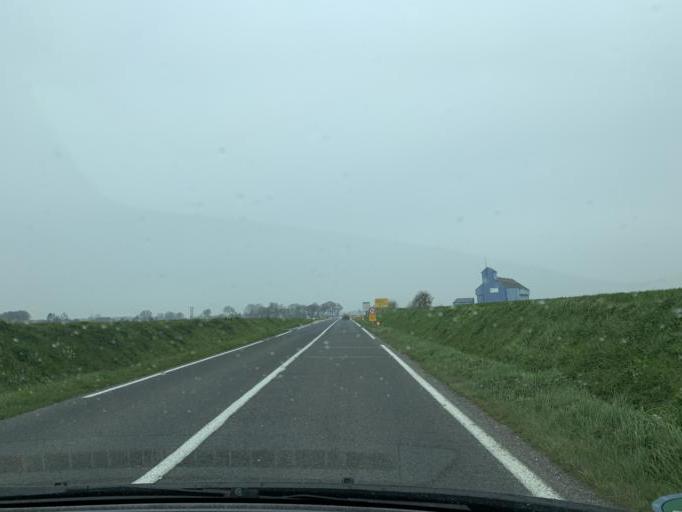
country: FR
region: Haute-Normandie
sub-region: Departement de la Seine-Maritime
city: Neville
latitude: 49.8158
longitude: 0.6705
